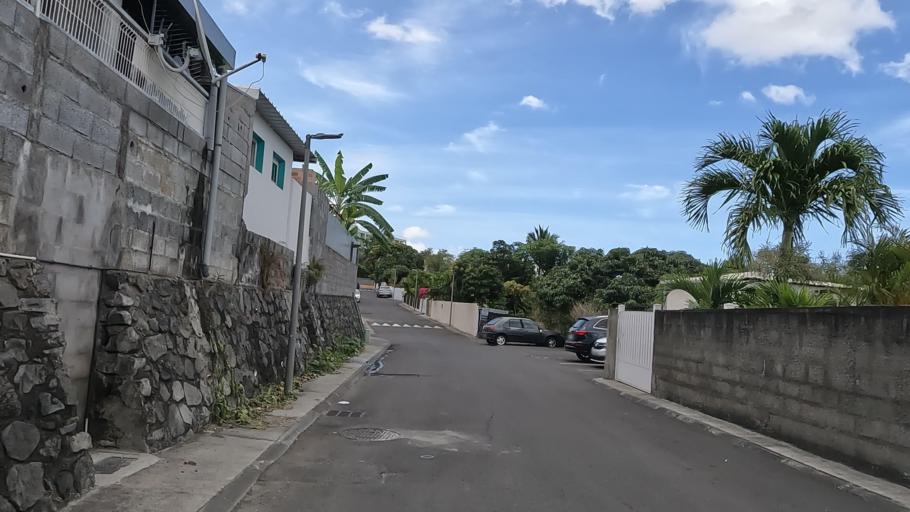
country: RE
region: Reunion
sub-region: Reunion
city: La Possession
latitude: -20.9479
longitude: 55.3308
